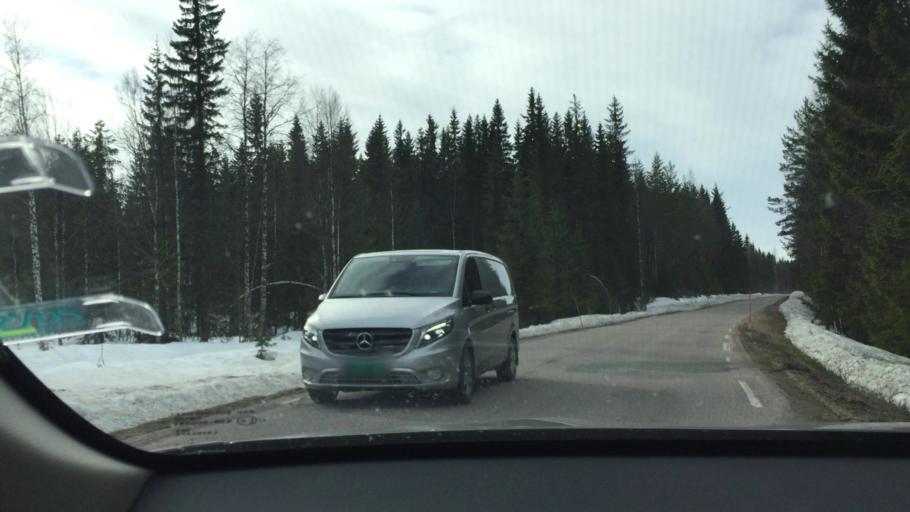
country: NO
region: Hedmark
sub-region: Trysil
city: Innbygda
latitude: 61.0670
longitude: 12.5458
